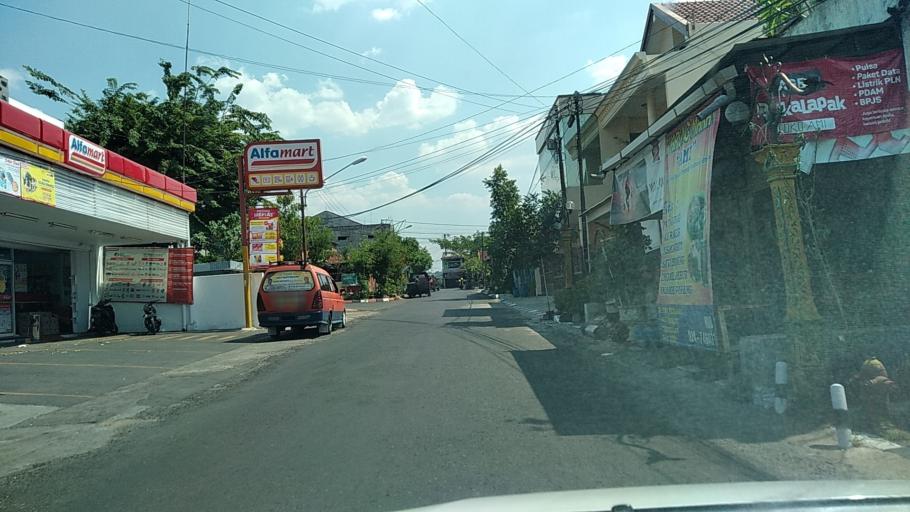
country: ID
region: Central Java
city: Ungaran
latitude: -7.0735
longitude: 110.4308
